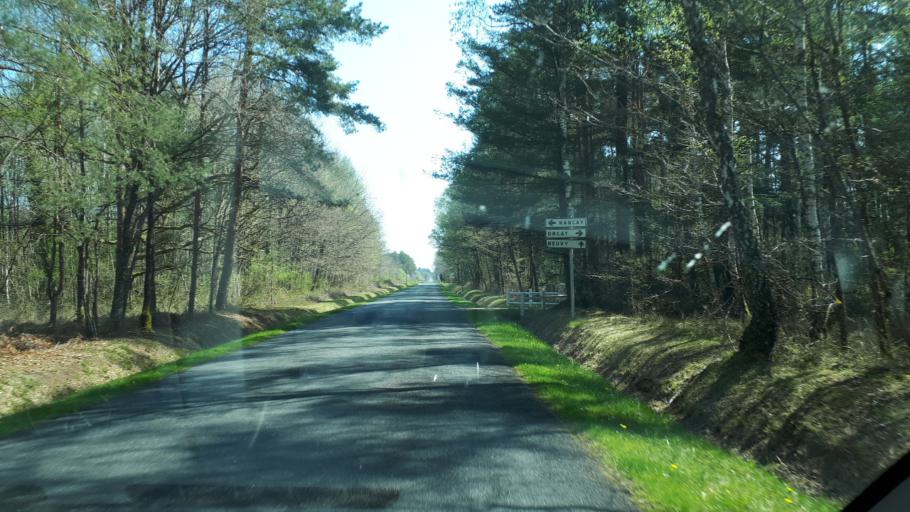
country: FR
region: Centre
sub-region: Departement du Loir-et-Cher
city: Theillay
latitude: 47.3175
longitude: 2.1444
